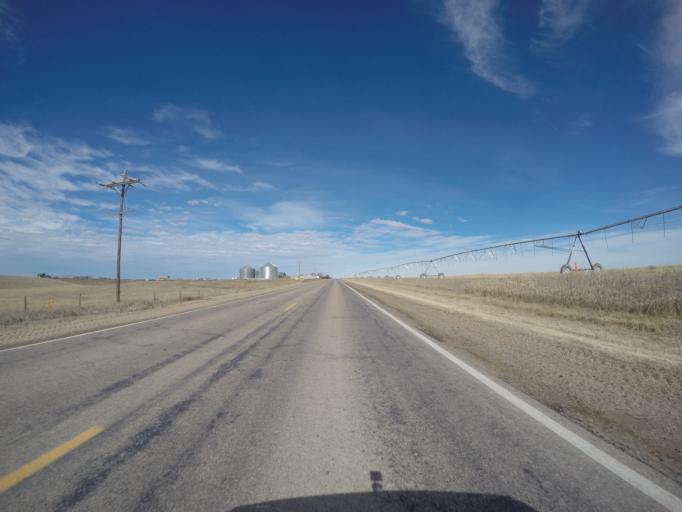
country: US
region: Nebraska
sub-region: Franklin County
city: Franklin
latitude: 40.1197
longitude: -98.9523
